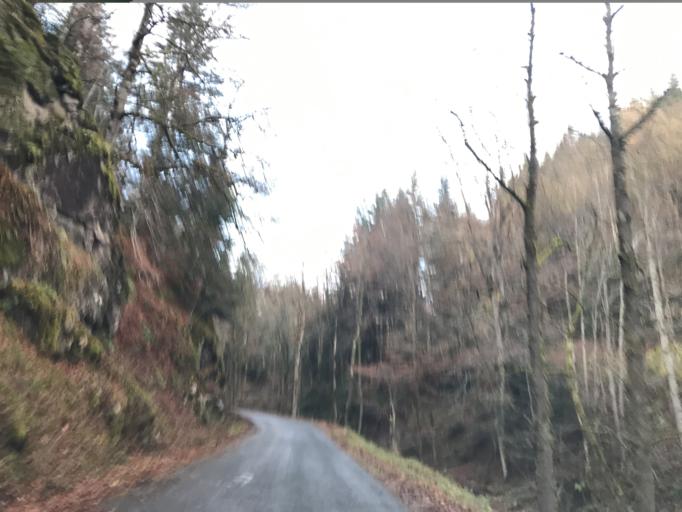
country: FR
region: Auvergne
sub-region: Departement du Puy-de-Dome
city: Courpiere
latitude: 45.7613
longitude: 3.6318
